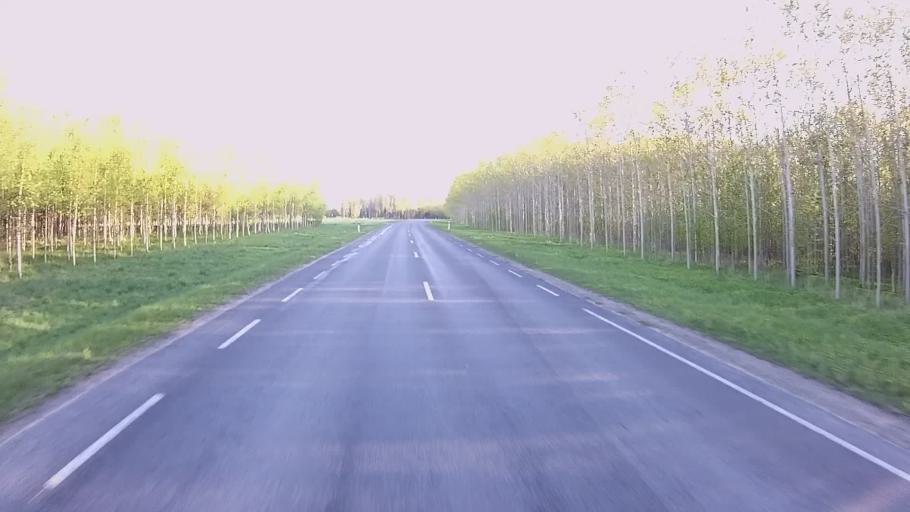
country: EE
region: Viljandimaa
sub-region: Viiratsi vald
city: Viiratsi
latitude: 58.4415
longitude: 25.7335
